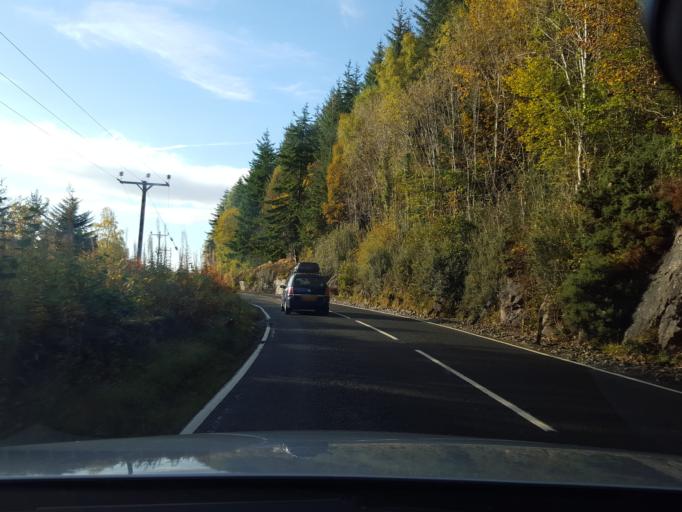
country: GB
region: Scotland
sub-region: Highland
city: Beauly
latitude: 57.2348
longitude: -4.5599
